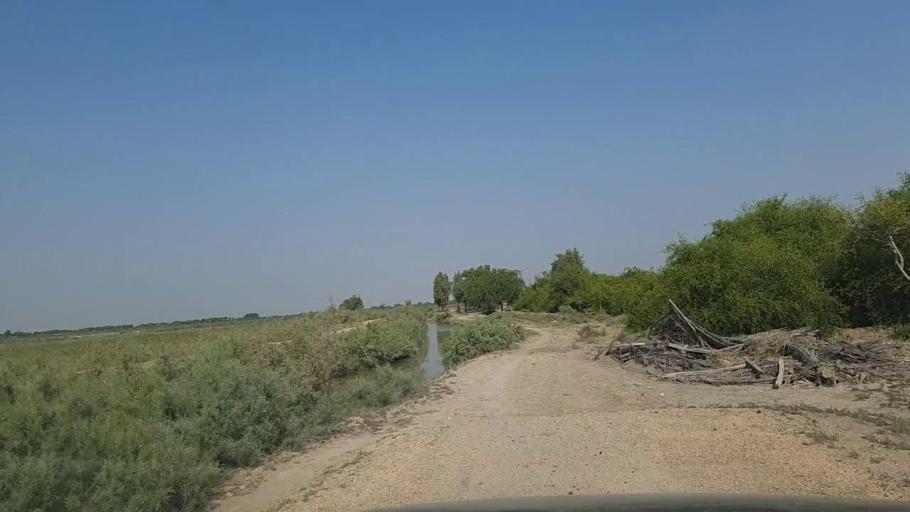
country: PK
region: Sindh
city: Mirpur Sakro
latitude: 24.5092
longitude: 67.7800
